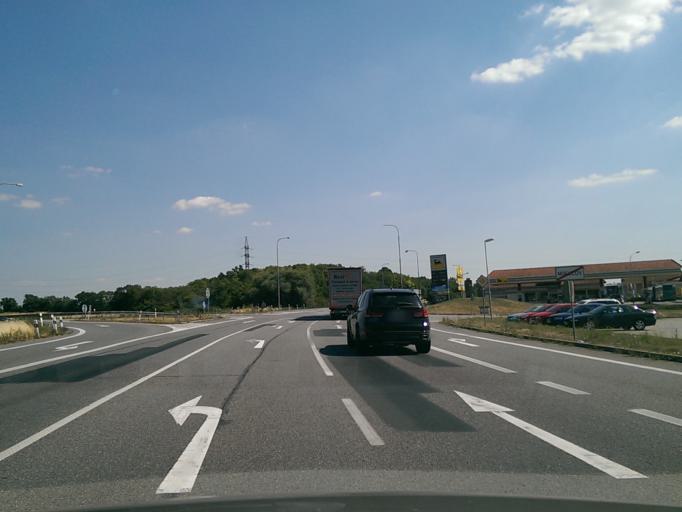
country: CZ
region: South Moravian
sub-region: Okres Breclav
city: Mikulov
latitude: 48.7994
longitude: 16.6323
